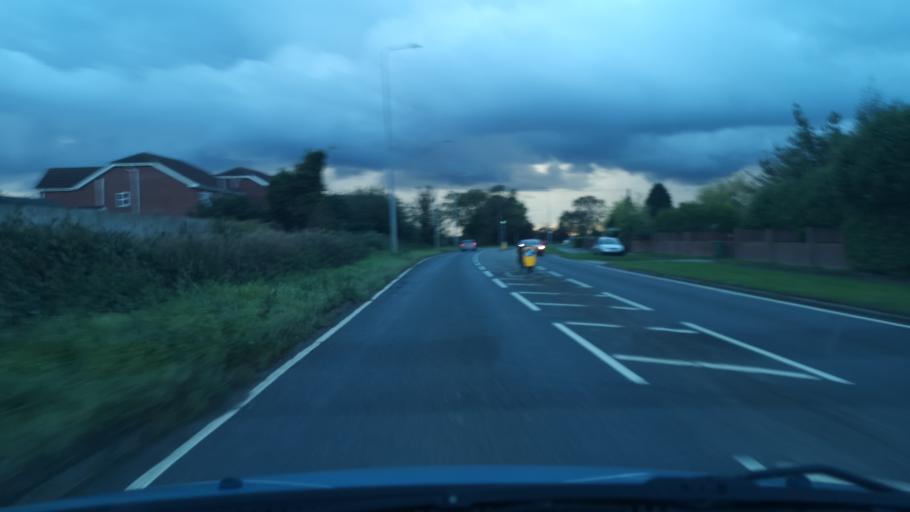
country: GB
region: England
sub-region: North Lincolnshire
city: Gunness
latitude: 53.5788
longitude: -0.7424
